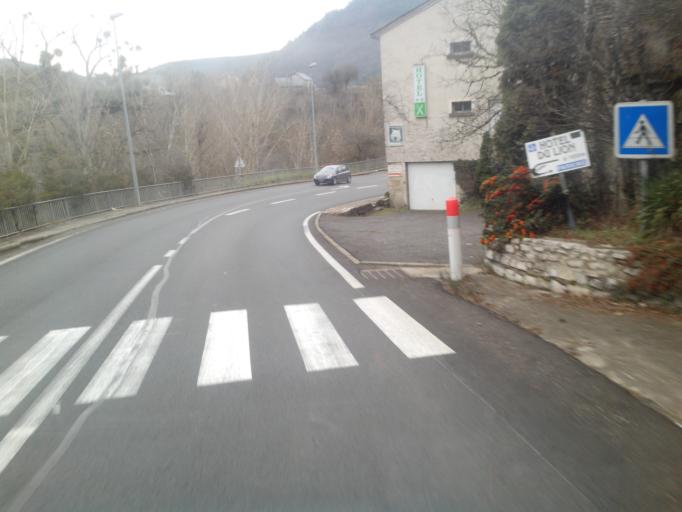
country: FR
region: Languedoc-Roussillon
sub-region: Departement de la Lozere
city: Mende
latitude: 44.4833
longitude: 3.4575
